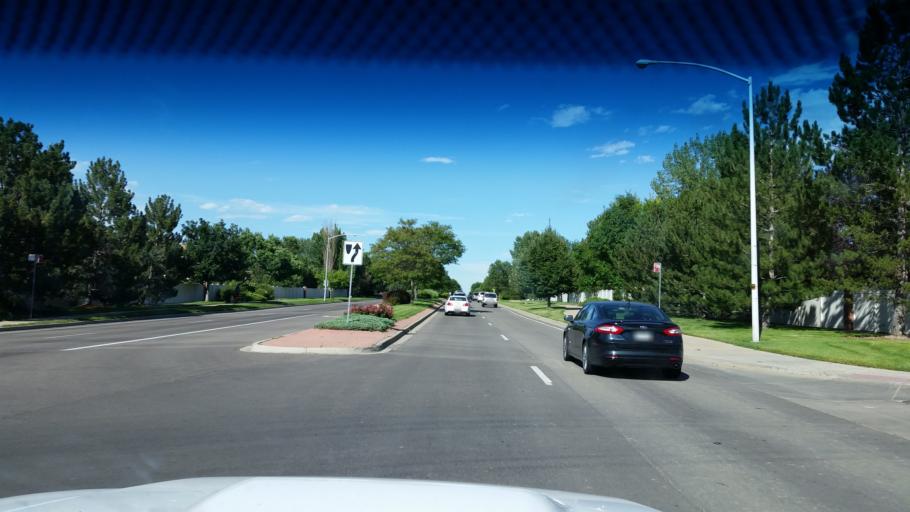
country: US
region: Colorado
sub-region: Broomfield County
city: Broomfield
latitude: 39.9254
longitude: -105.0511
